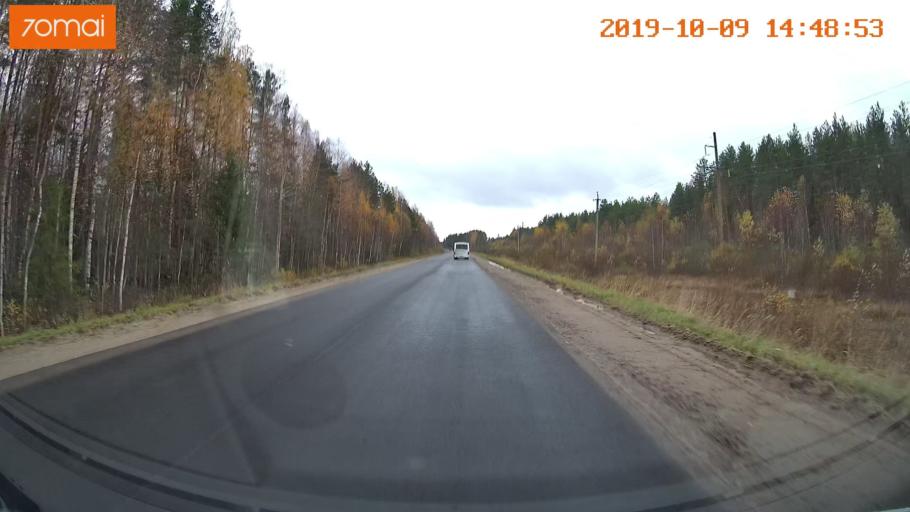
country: RU
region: Kostroma
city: Chistyye Bory
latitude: 58.4002
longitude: 41.5776
